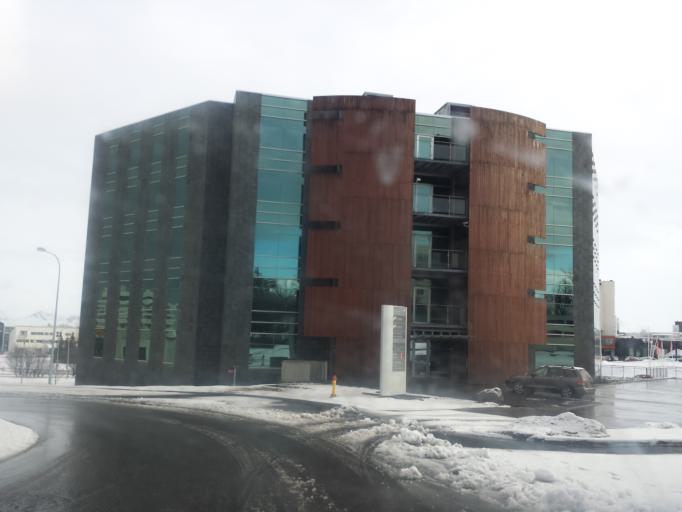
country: IS
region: Capital Region
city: Reykjavik
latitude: 64.1394
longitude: -21.8954
